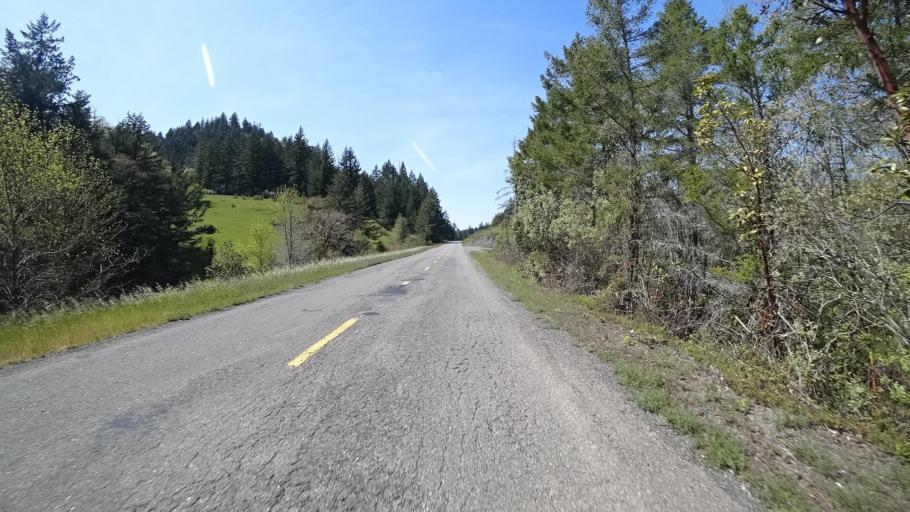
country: US
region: California
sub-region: Humboldt County
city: Redway
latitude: 40.3276
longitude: -123.6670
